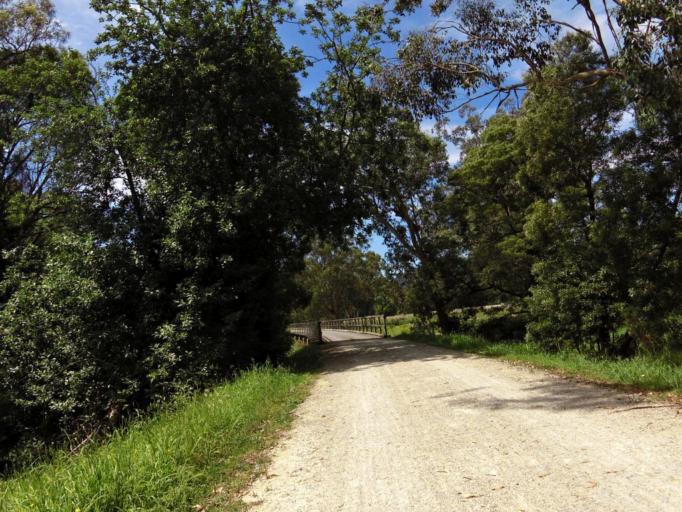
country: AU
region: Victoria
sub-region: Yarra Ranges
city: Yarra Junction
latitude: -37.7810
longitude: 145.6210
